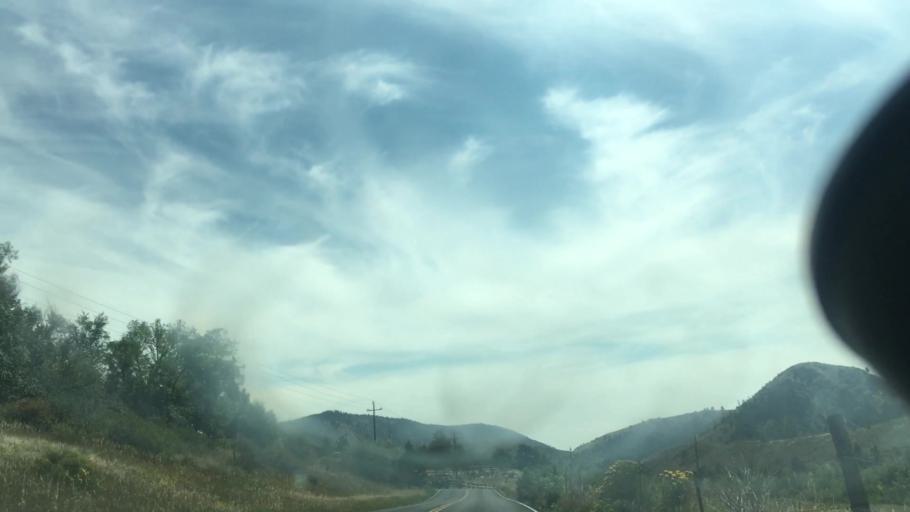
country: US
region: Colorado
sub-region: Larimer County
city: Laporte
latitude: 40.5711
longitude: -105.3213
